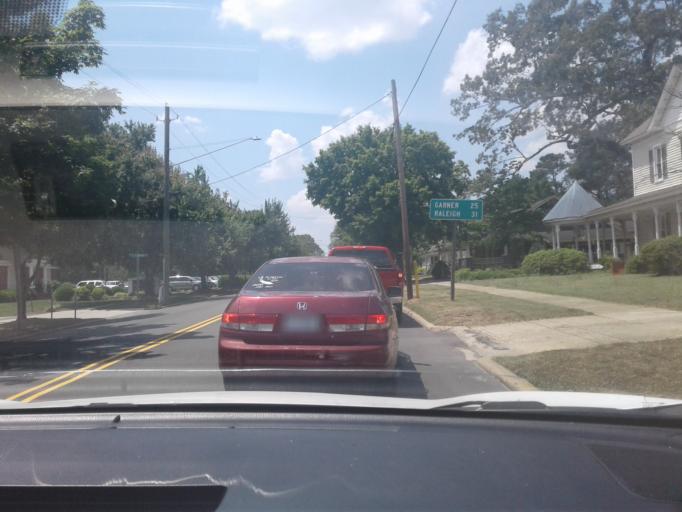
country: US
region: North Carolina
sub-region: Johnston County
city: Benson
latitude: 35.3828
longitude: -78.5503
